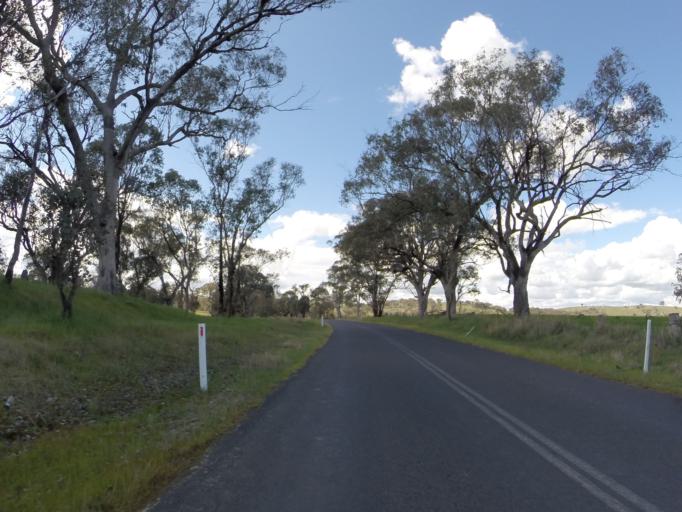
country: AU
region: New South Wales
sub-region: Yass Valley
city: Yass
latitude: -34.9837
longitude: 148.8517
